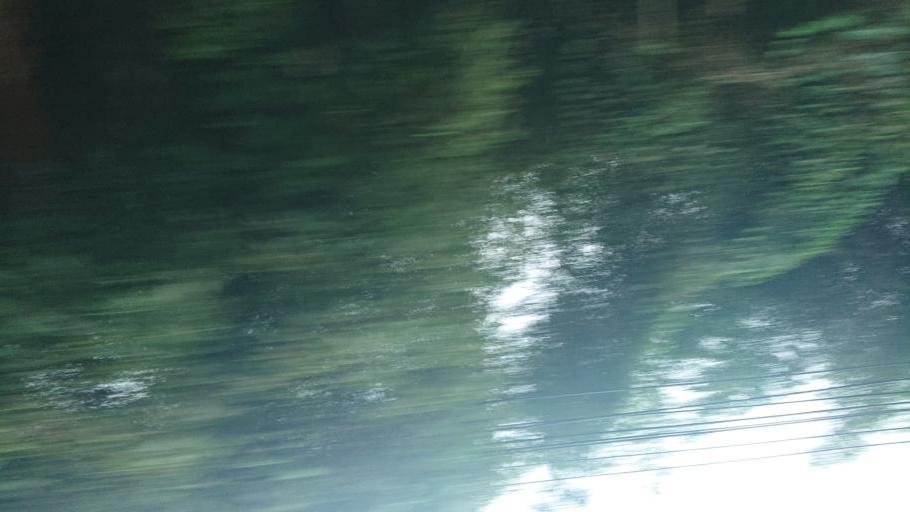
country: TW
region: Taiwan
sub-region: Chiayi
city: Jiayi Shi
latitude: 23.4783
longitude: 120.7157
